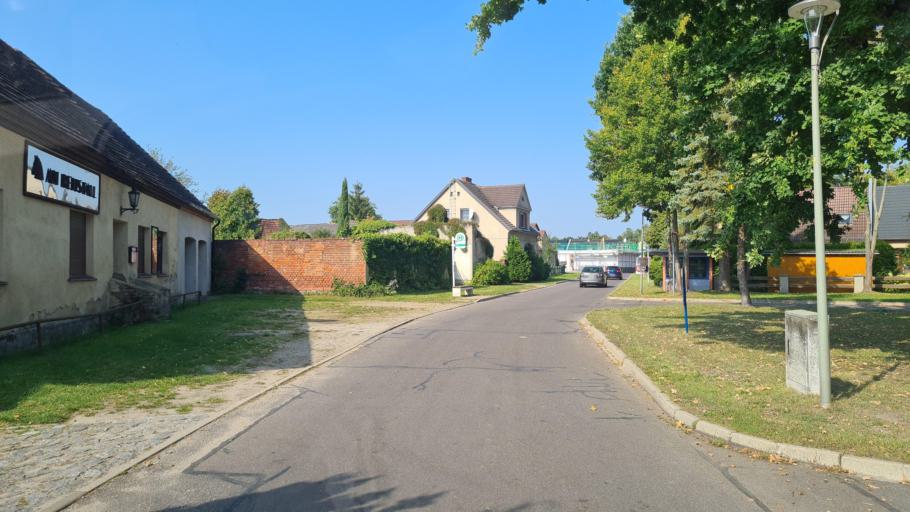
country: DE
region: Brandenburg
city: Kolkwitz
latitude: 51.7483
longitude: 14.2063
